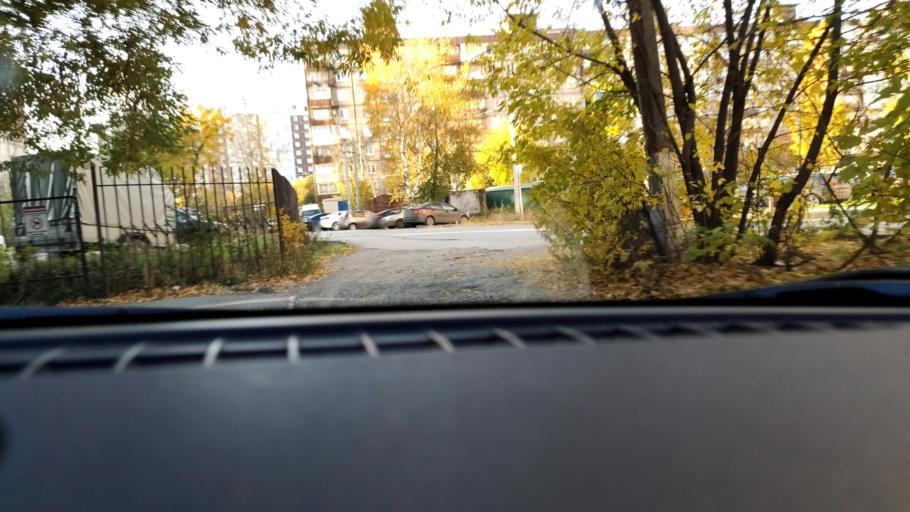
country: RU
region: Perm
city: Kondratovo
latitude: 57.9997
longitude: 56.1521
